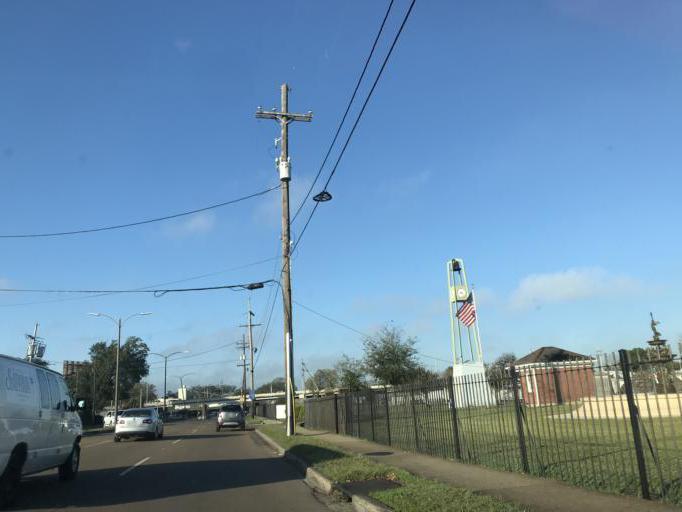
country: US
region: Louisiana
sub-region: Jefferson Parish
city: Metairie
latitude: 29.9818
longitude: -90.1117
